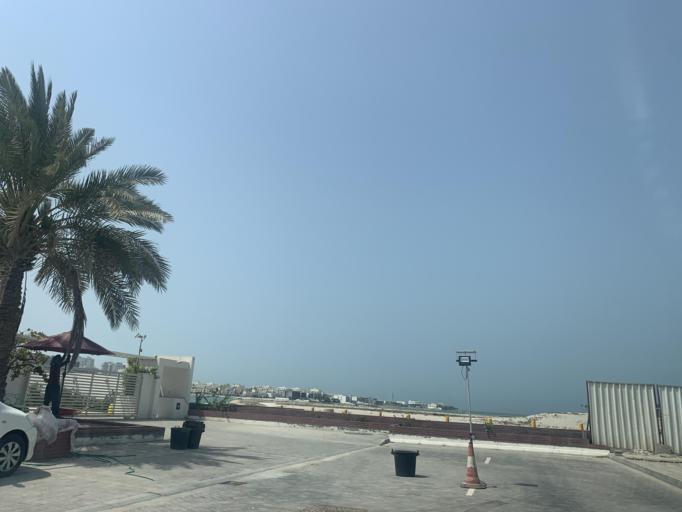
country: BH
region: Muharraq
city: Al Hadd
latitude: 26.2756
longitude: 50.6719
